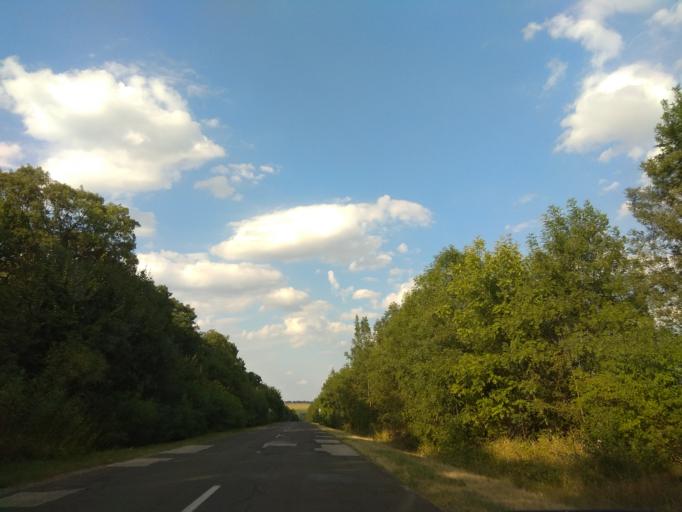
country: HU
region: Borsod-Abauj-Zemplen
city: Harsany
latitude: 47.9312
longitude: 20.7302
